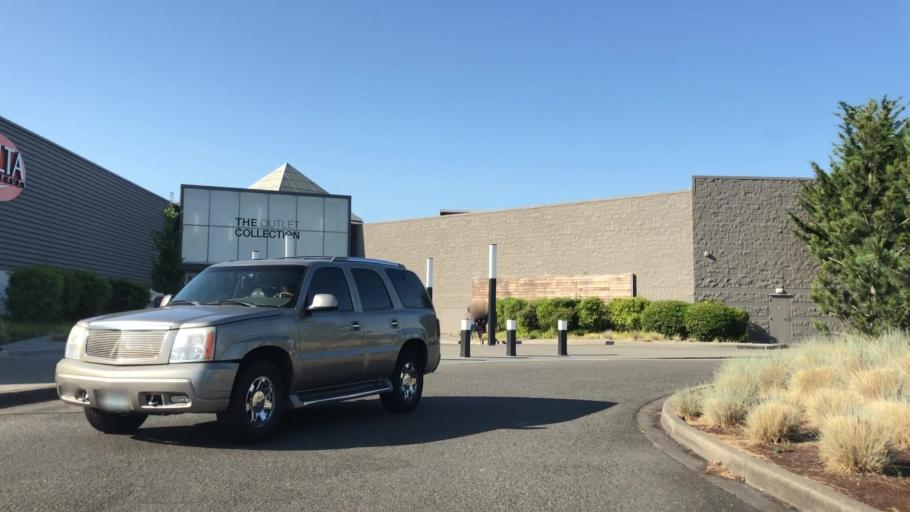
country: US
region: Washington
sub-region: King County
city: Auburn
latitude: 47.2976
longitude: -122.2438
